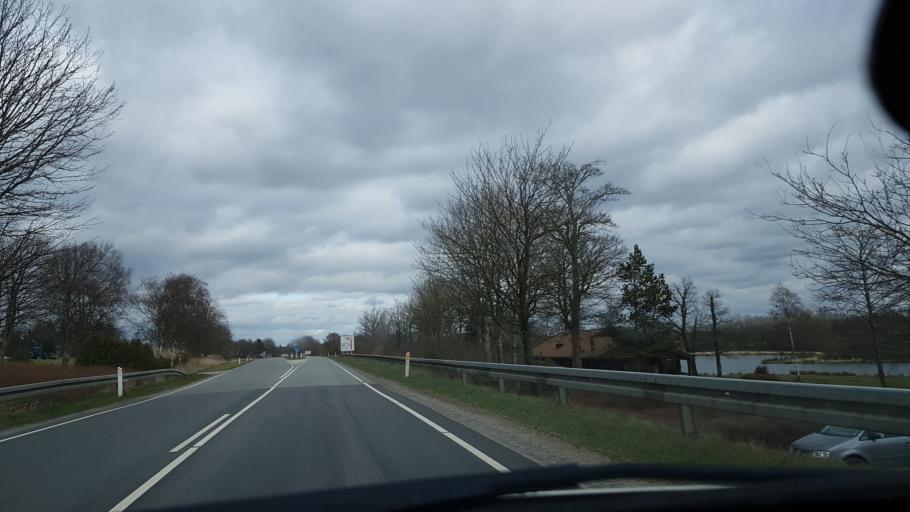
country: DK
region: South Denmark
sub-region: Vejen Kommune
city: Holsted
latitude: 55.4357
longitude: 8.9126
